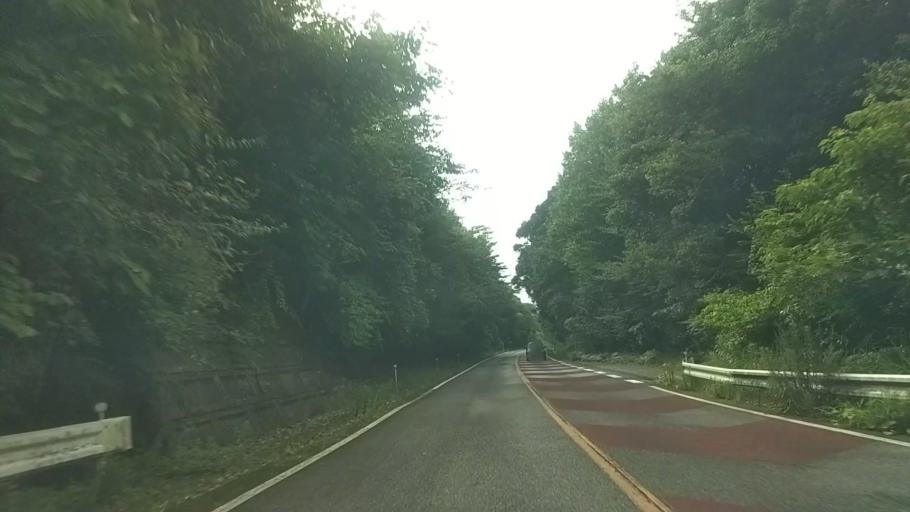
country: JP
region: Chiba
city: Kawaguchi
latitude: 35.2318
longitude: 140.0228
